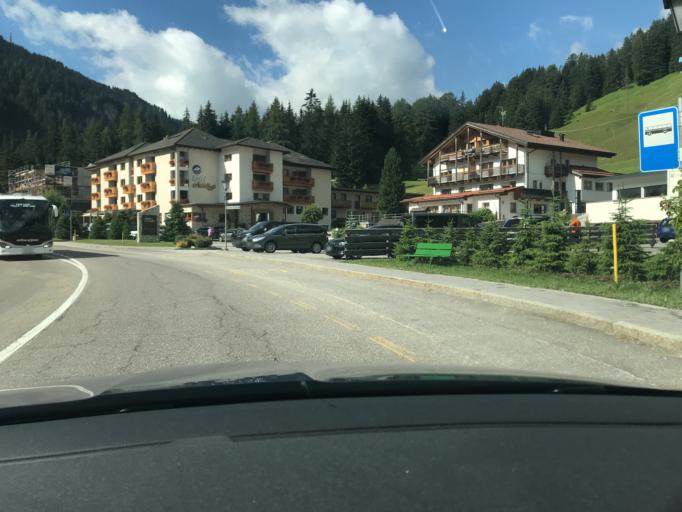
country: IT
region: Trentino-Alto Adige
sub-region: Bolzano
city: Corvara in Badia
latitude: 46.5674
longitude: 11.8873
